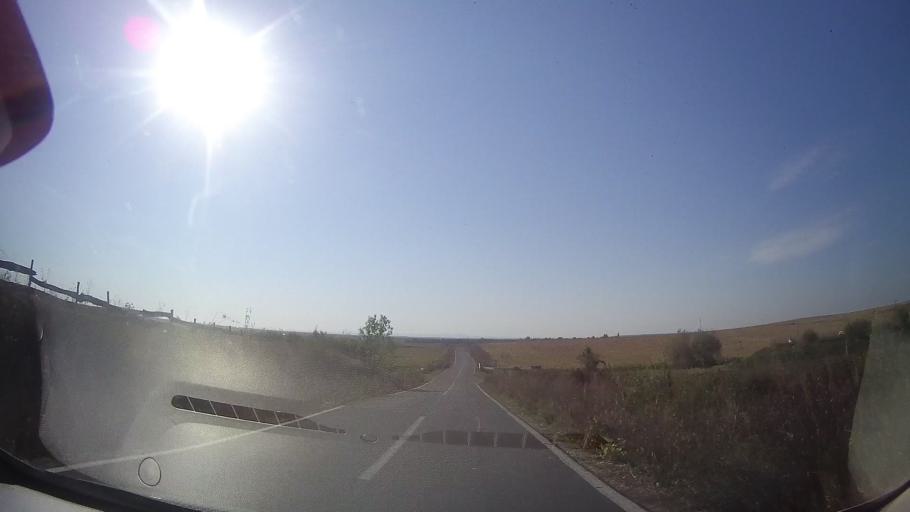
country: RO
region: Timis
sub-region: Comuna Topolovatu Mare
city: Topolovatu Mare
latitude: 45.8020
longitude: 21.5857
